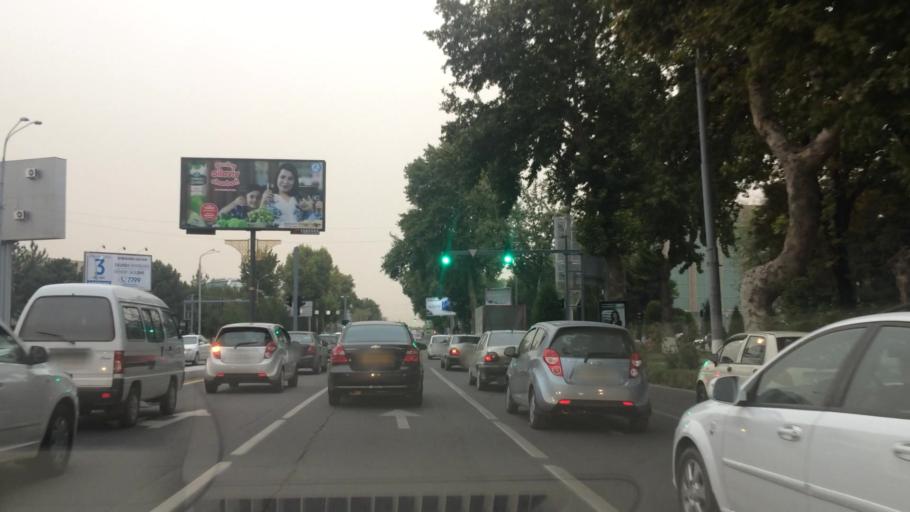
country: UZ
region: Toshkent Shahri
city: Tashkent
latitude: 41.3035
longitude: 69.2800
